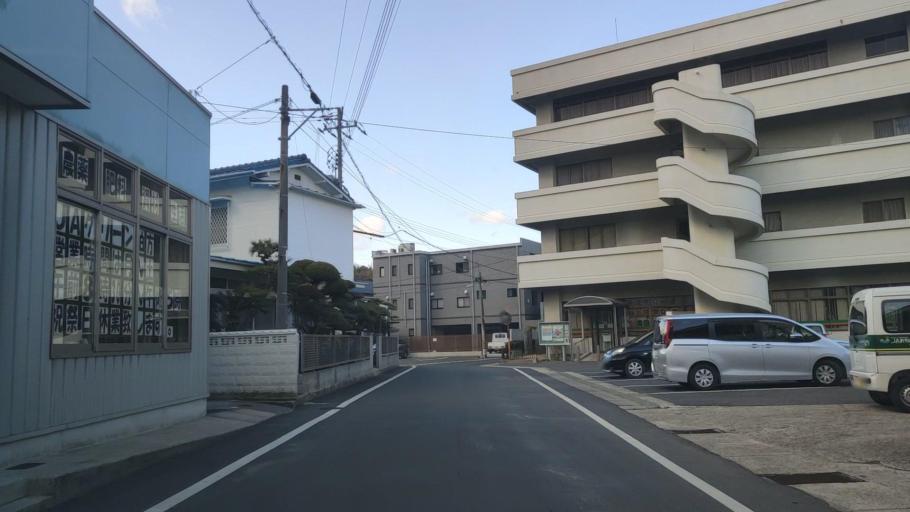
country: JP
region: Hiroshima
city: Innoshima
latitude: 34.2040
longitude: 133.1171
